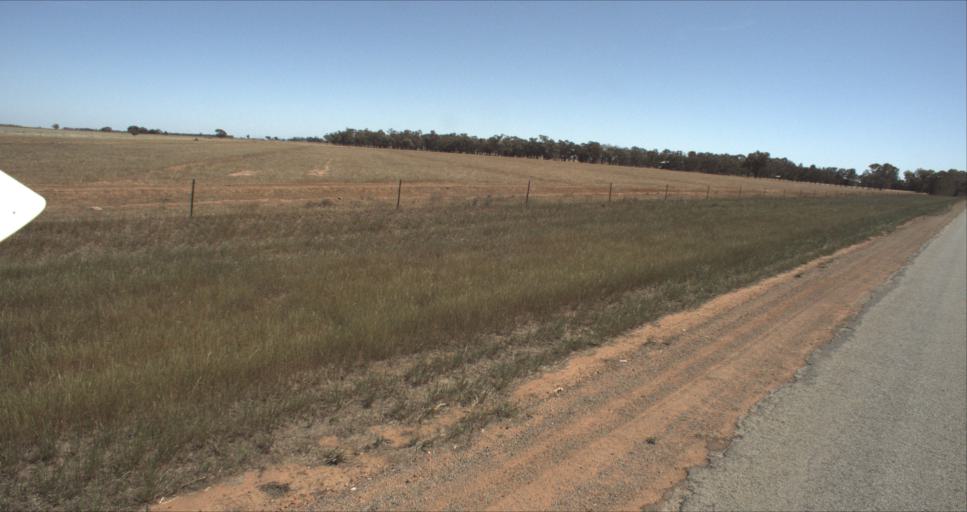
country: AU
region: New South Wales
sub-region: Leeton
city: Leeton
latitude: -34.5808
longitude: 146.3088
